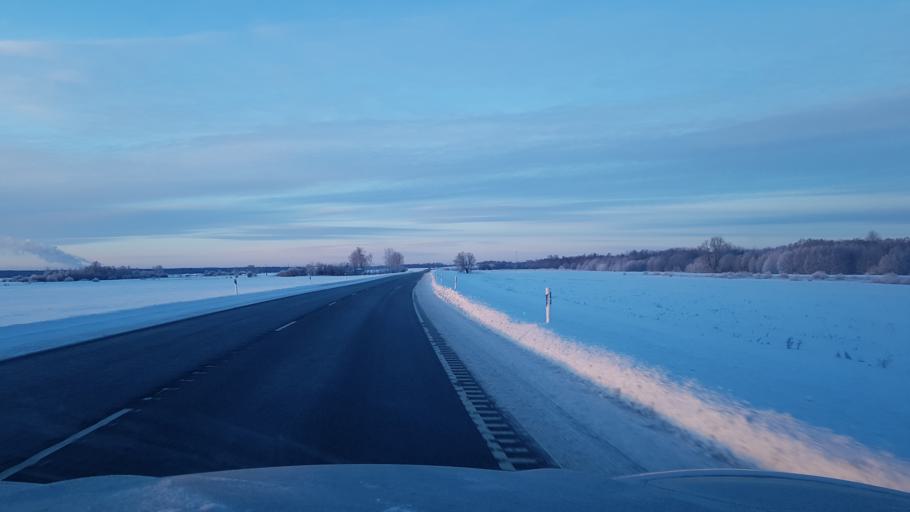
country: EE
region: Ida-Virumaa
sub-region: Narva-Joesuu linn
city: Narva-Joesuu
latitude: 59.4014
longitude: 28.0140
